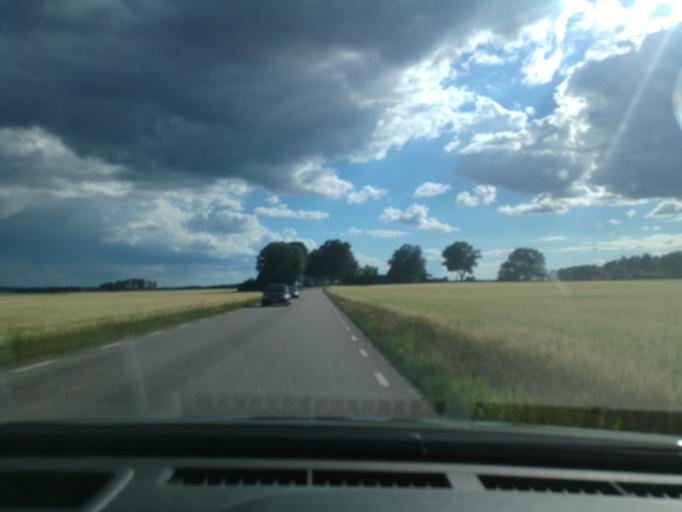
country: SE
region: Soedermanland
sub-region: Eskilstuna Kommun
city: Arla
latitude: 59.4398
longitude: 16.7164
